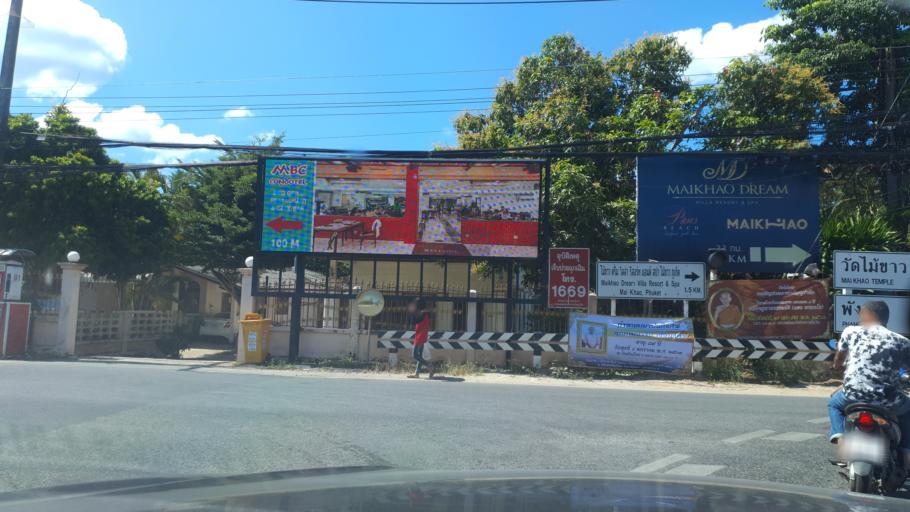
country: TH
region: Phuket
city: Thalang
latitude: 8.1216
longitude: 98.3085
